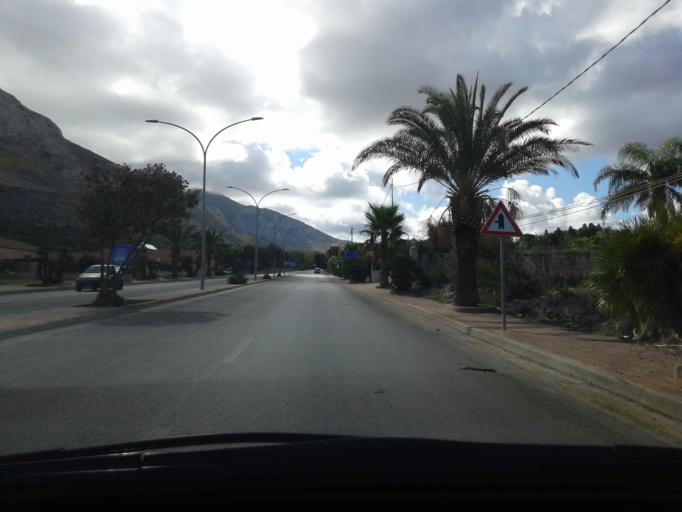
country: IT
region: Sicily
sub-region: Trapani
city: San Vito Lo Capo
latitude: 38.1611
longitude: 12.7368
